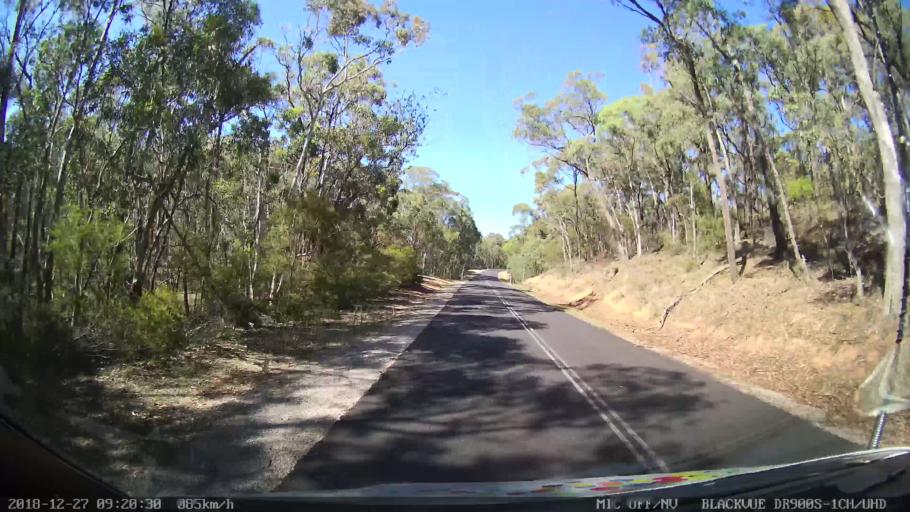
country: AU
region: New South Wales
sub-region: Lithgow
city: Portland
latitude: -33.1199
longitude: 150.0221
